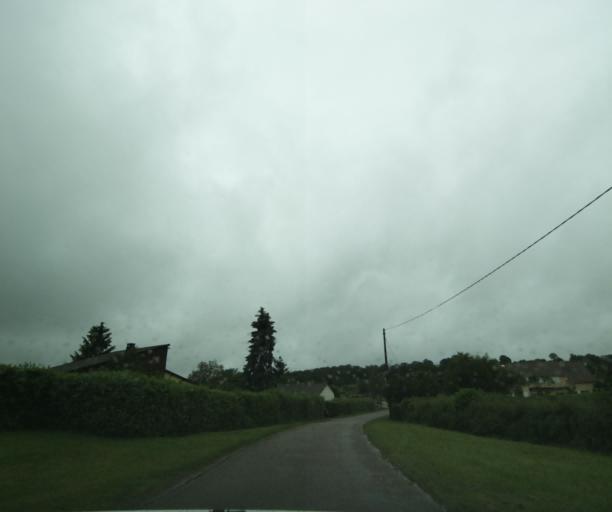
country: FR
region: Bourgogne
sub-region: Departement de Saone-et-Loire
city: Charolles
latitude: 46.4143
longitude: 4.3051
